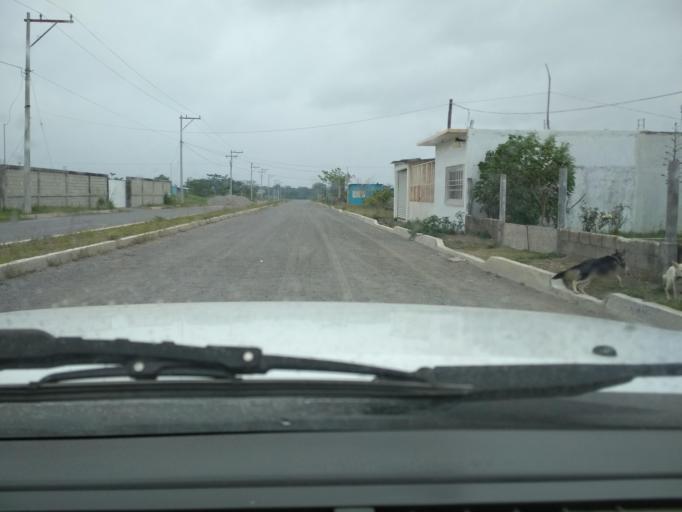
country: MX
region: Veracruz
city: Paso del Toro
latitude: 19.0429
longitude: -96.1337
